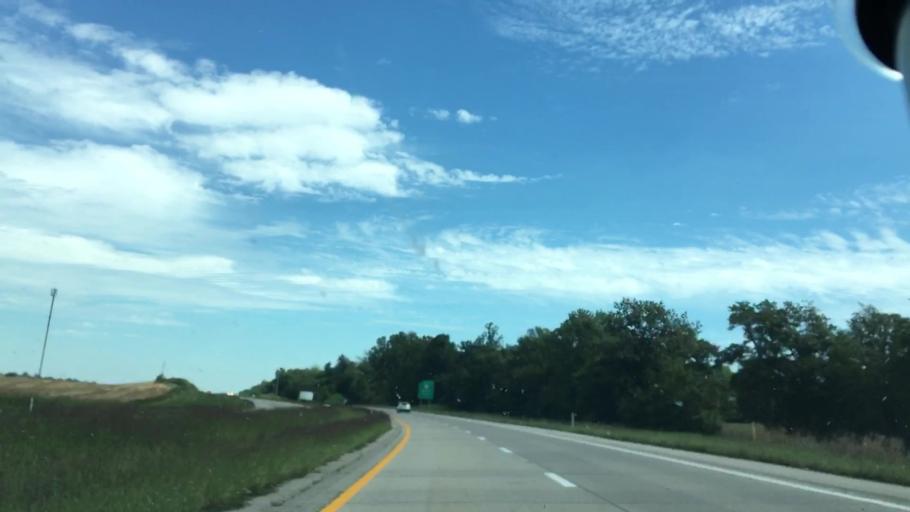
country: US
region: Kentucky
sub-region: Daviess County
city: Owensboro
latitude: 37.7512
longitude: -87.2862
